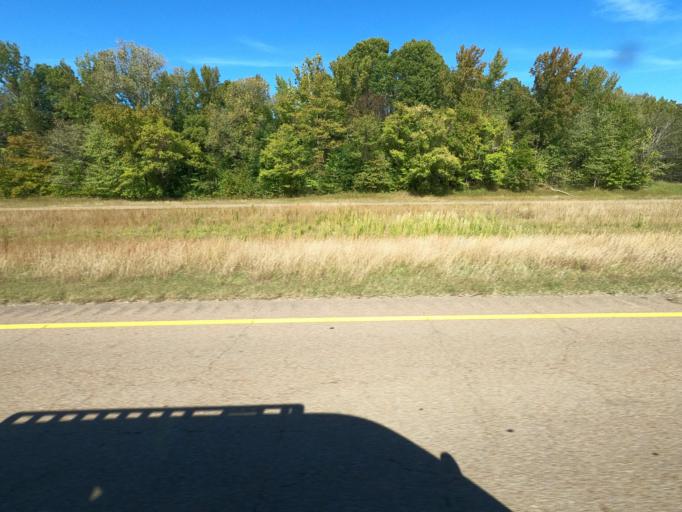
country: US
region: Tennessee
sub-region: Dyer County
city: Dyersburg
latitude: 36.0693
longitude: -89.4411
